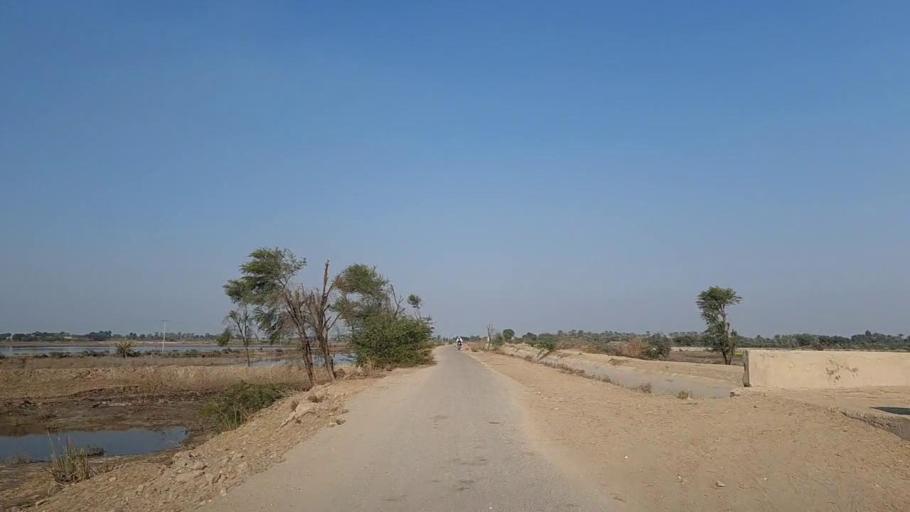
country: PK
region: Sindh
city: Daur
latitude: 26.4291
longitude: 68.2650
